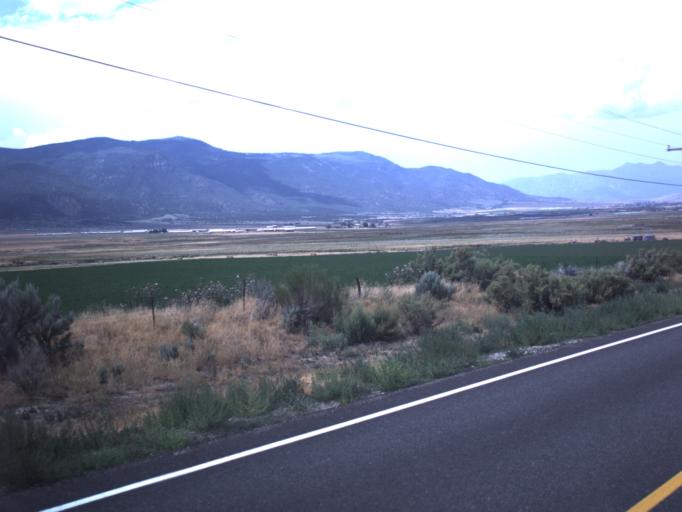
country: US
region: Utah
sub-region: Sanpete County
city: Moroni
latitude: 39.5524
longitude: -111.6000
